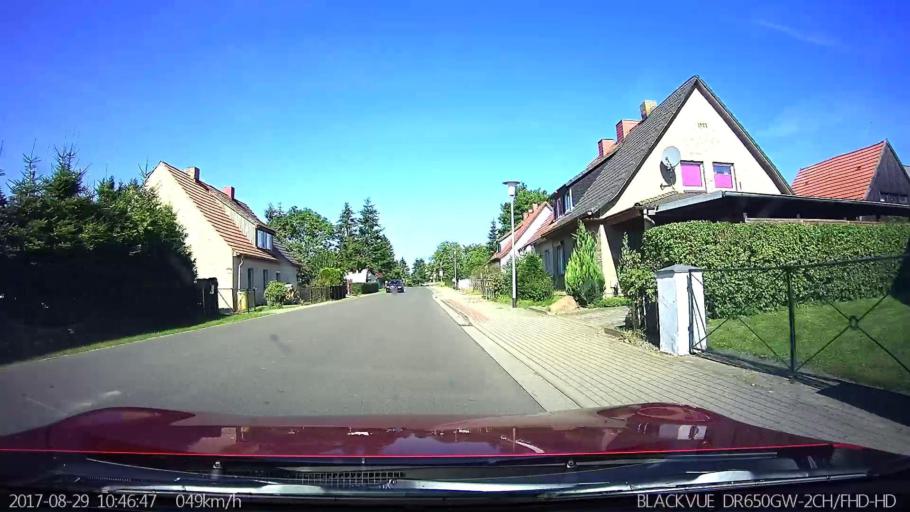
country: DE
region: Mecklenburg-Vorpommern
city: Velgast
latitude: 54.2231
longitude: 12.8361
